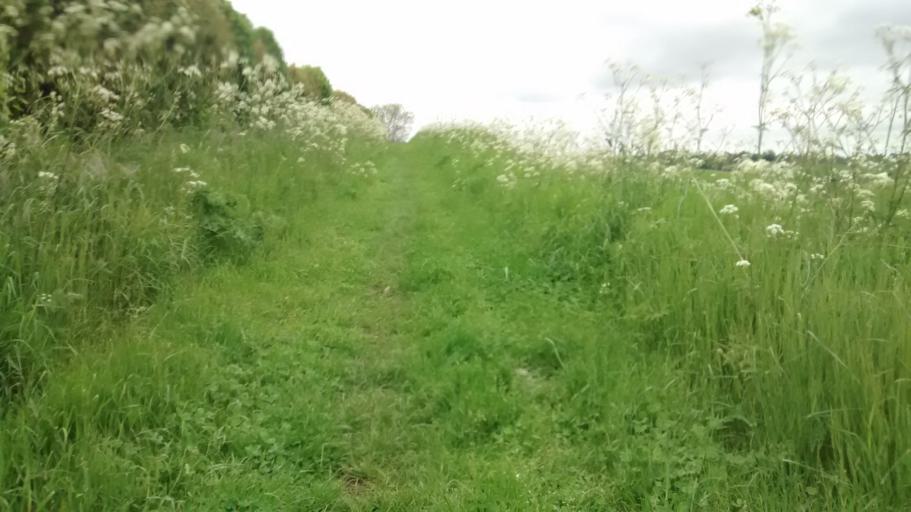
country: GB
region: England
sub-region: County Durham
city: Pittington
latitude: 54.7848
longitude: -1.5063
